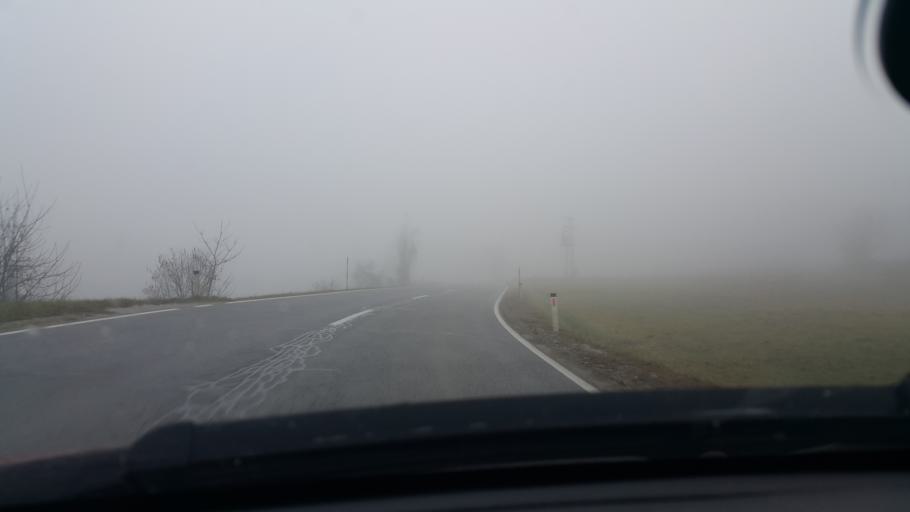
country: SI
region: Bistrica ob Sotli
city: Bistrica ob Sotli
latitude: 45.9982
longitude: 15.6937
